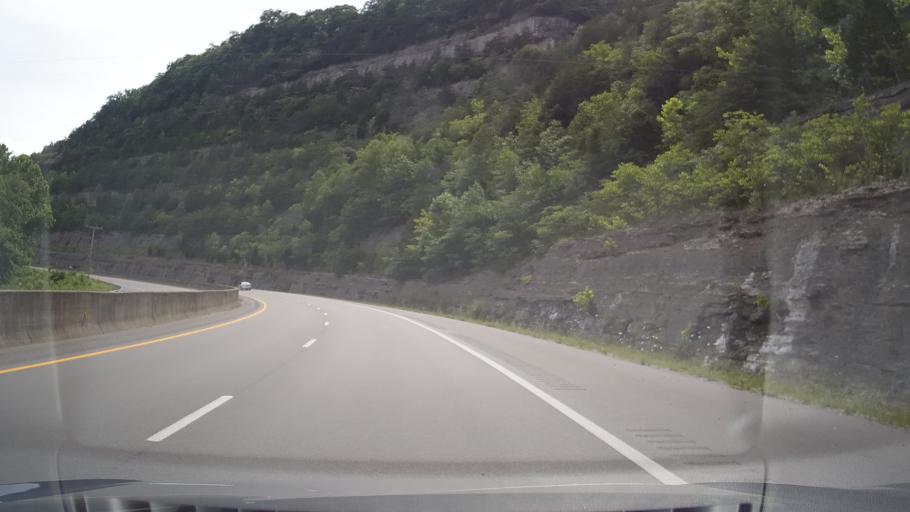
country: US
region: Kentucky
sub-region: Pike County
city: Coal Run Village
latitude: 37.5376
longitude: -82.6143
